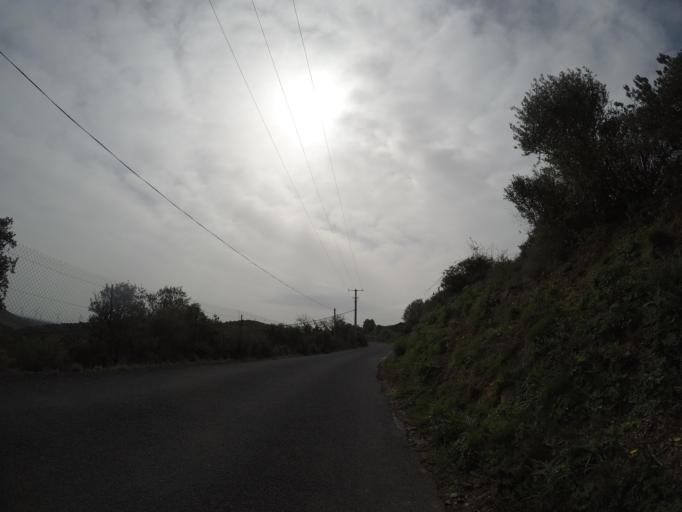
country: FR
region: Languedoc-Roussillon
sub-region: Departement des Pyrenees-Orientales
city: Corneilla-la-Riviere
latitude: 42.7300
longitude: 2.7388
